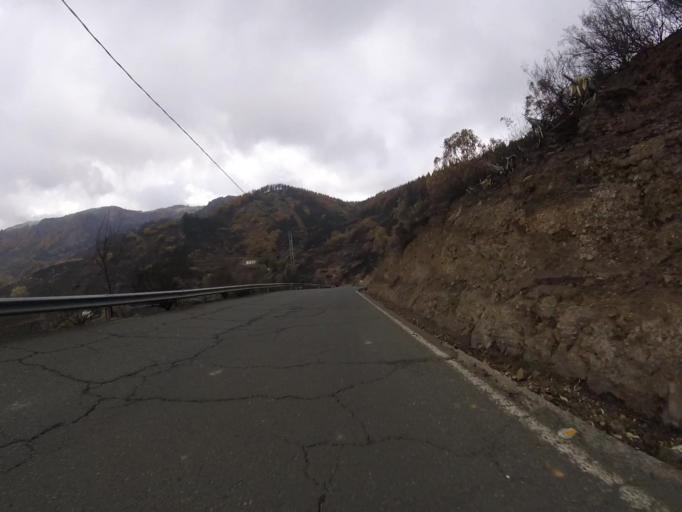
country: ES
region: Canary Islands
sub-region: Provincia de Las Palmas
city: Tejeda
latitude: 27.9868
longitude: -15.5758
